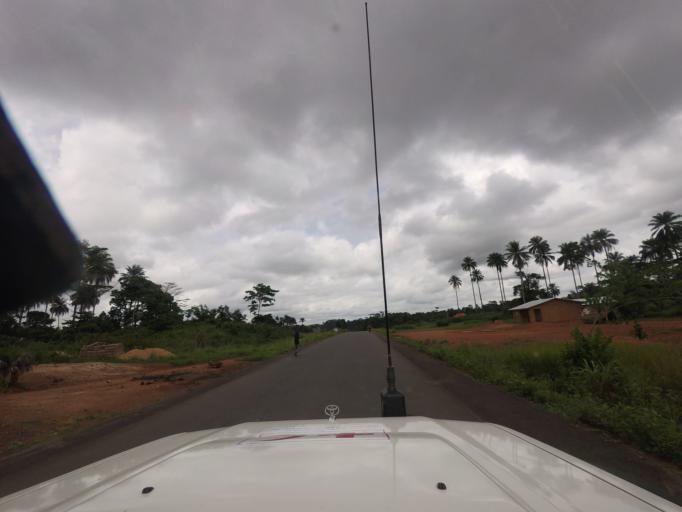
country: GN
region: Nzerekore
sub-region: Macenta
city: Macenta
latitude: 8.2853
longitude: -9.1795
